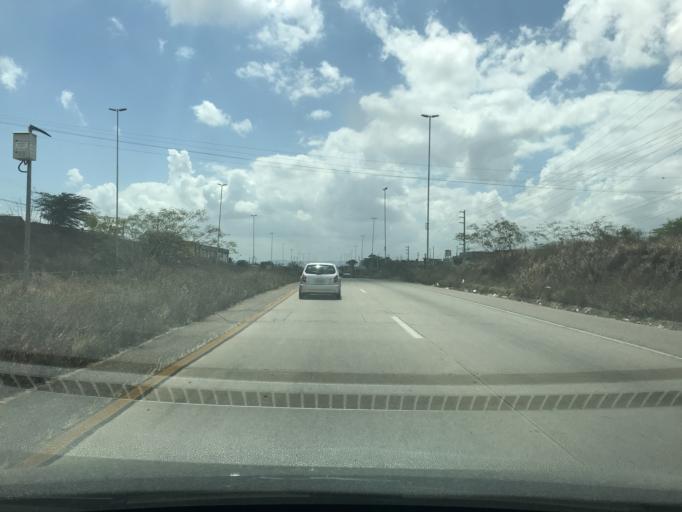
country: BR
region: Pernambuco
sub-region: Caruaru
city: Caruaru
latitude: -8.3037
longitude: -35.9736
